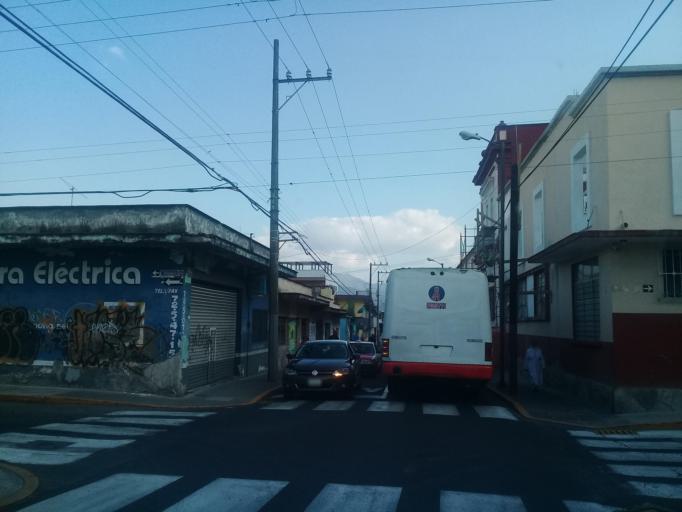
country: MX
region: Veracruz
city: Orizaba
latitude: 18.8487
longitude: -97.1108
